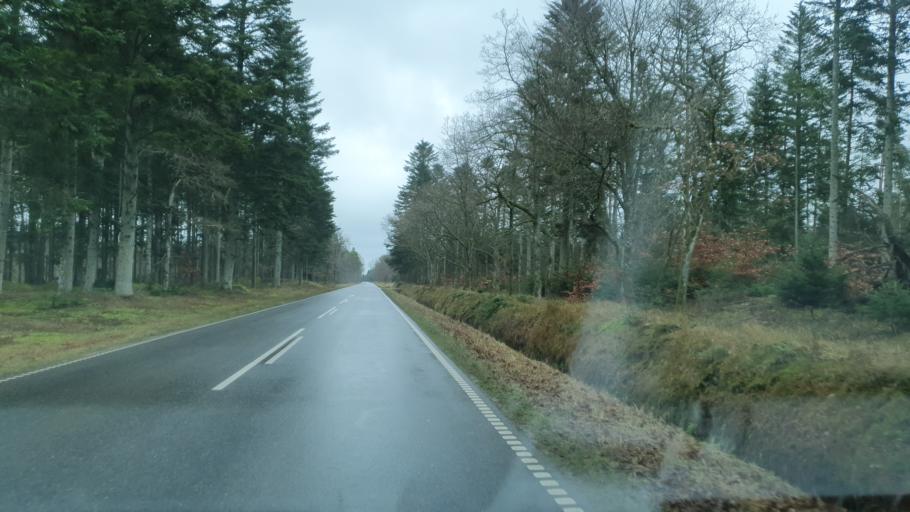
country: DK
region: North Denmark
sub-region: Jammerbugt Kommune
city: Fjerritslev
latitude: 57.1220
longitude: 9.1276
